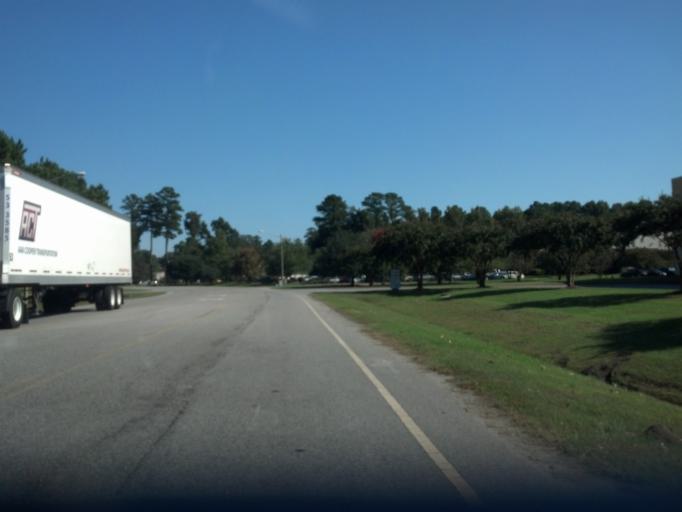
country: US
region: North Carolina
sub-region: Pitt County
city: Greenville
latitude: 35.6556
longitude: -77.3448
